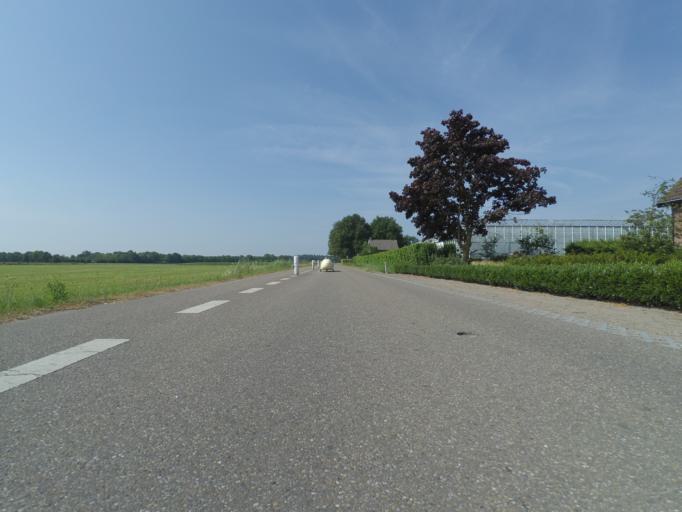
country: NL
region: North Brabant
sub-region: Gemeente Zundert
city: Zundert
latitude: 51.4931
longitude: 4.6286
